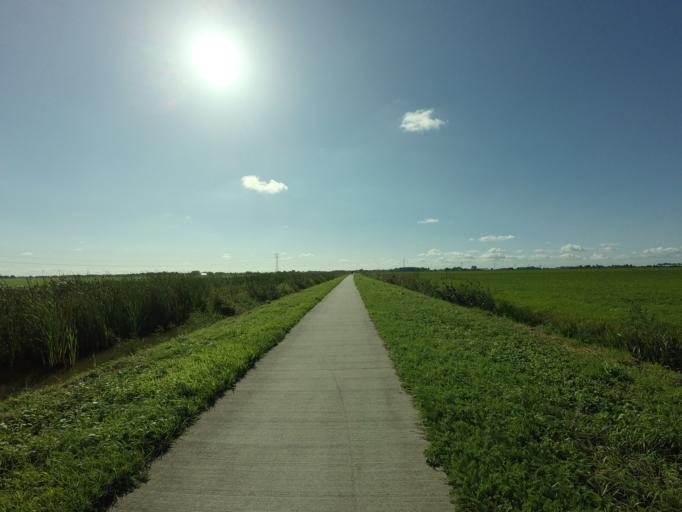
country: NL
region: Friesland
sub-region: Gemeente Boarnsterhim
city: Reduzum
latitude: 53.1198
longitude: 5.7559
